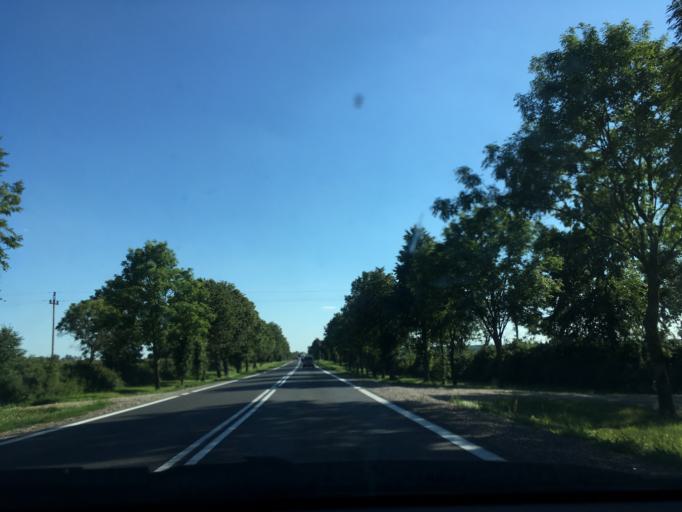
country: PL
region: Podlasie
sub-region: Powiat sokolski
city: Suchowola
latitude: 53.4756
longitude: 23.0913
